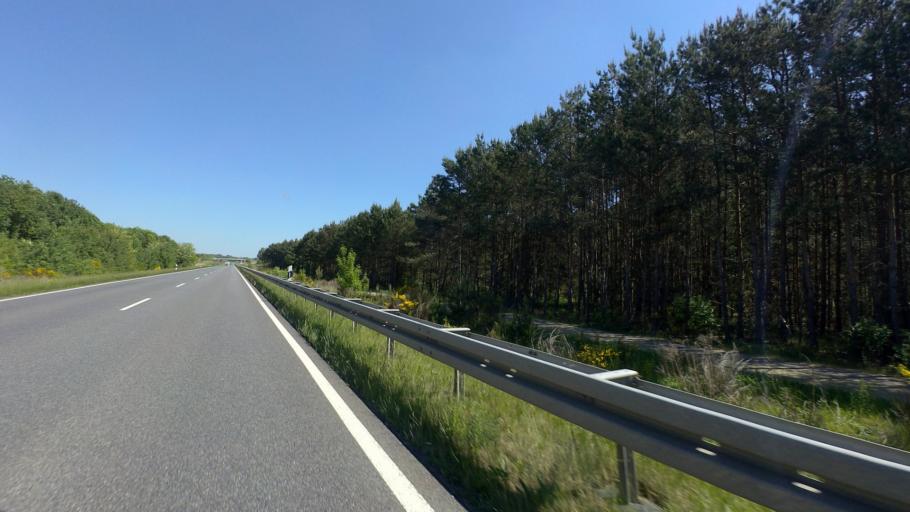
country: DE
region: Brandenburg
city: Spremberg
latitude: 51.5653
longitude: 14.3301
